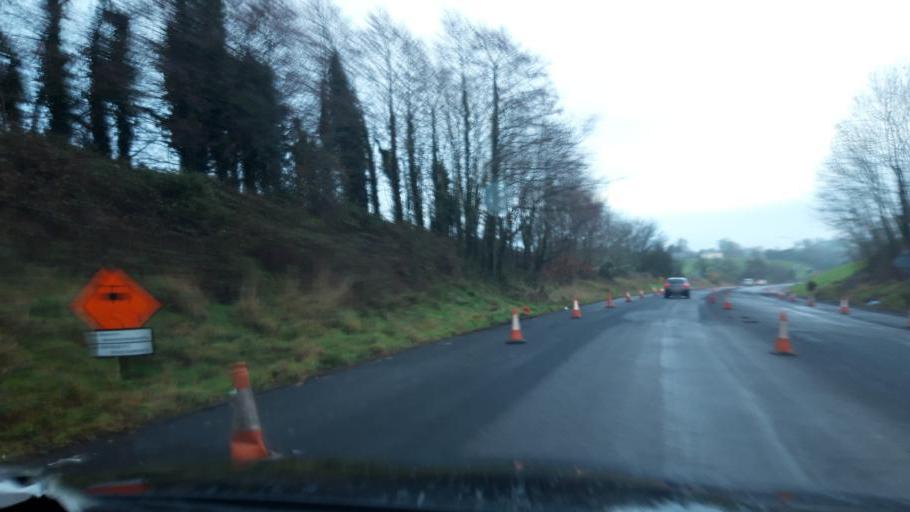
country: IE
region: Ulster
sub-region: County Donegal
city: Raphoe
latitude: 54.9408
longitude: -7.6207
